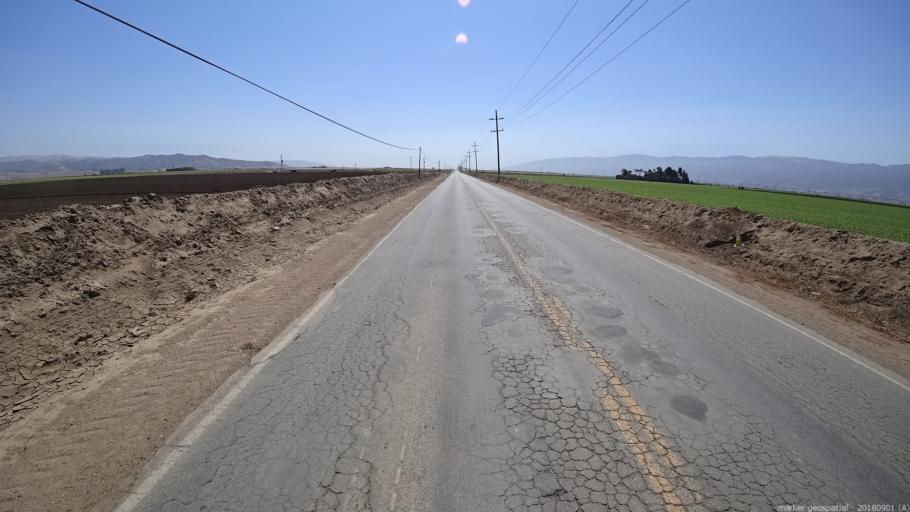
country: US
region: California
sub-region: Monterey County
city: Chualar
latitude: 36.6040
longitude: -121.5130
